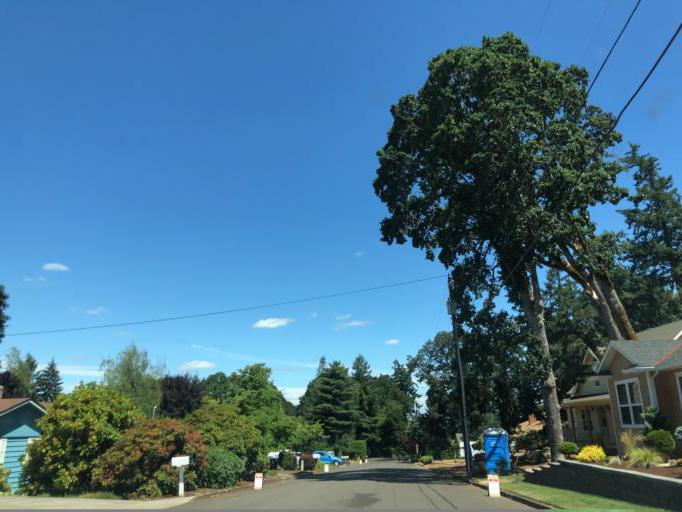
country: US
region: Oregon
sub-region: Marion County
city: Silverton
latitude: 44.9997
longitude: -122.7858
